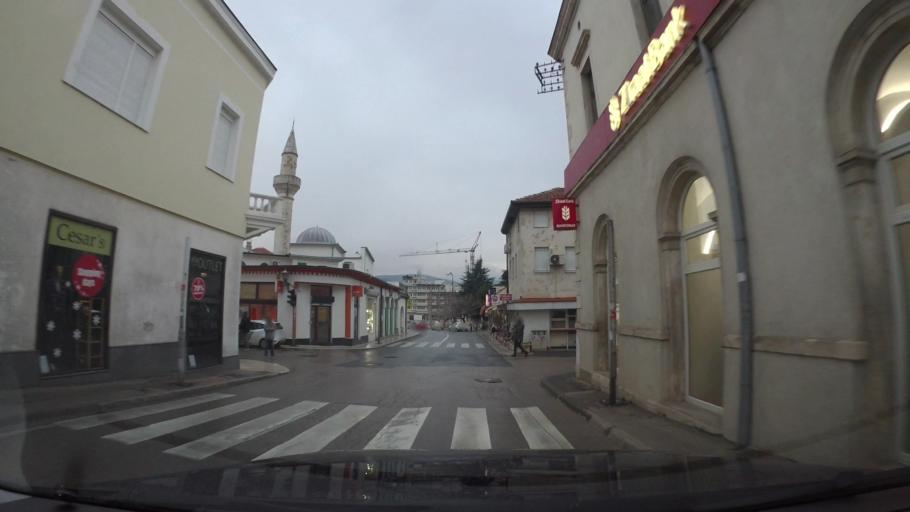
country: BA
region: Federation of Bosnia and Herzegovina
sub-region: Hercegovacko-Bosanski Kanton
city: Mostar
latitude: 43.3444
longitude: 17.8126
